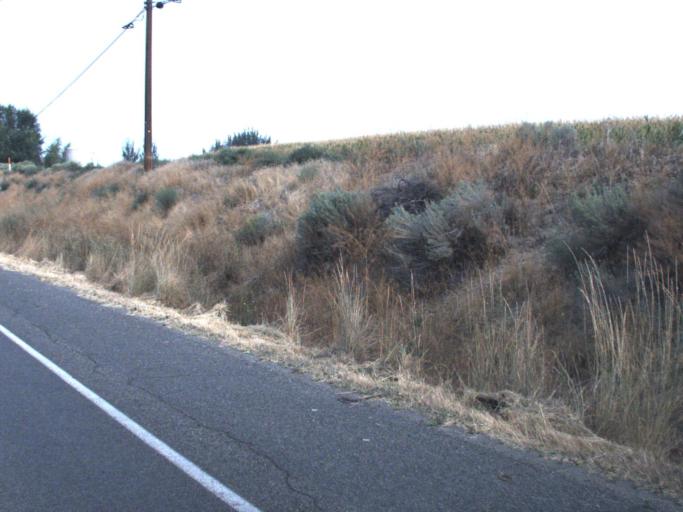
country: US
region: Washington
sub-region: Yakima County
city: Mabton
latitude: 46.2252
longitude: -119.9995
